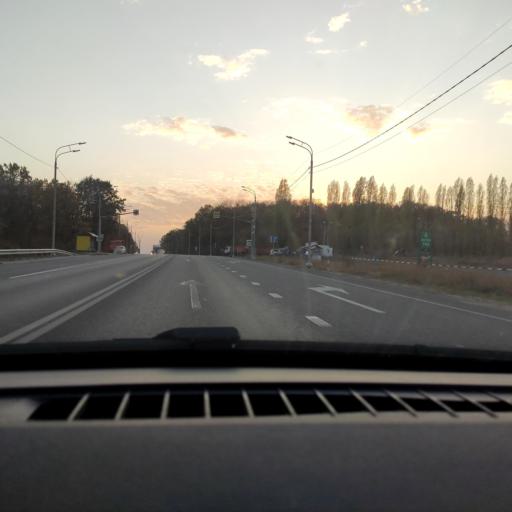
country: RU
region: Voronezj
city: Semiluki
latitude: 51.6498
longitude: 39.0313
